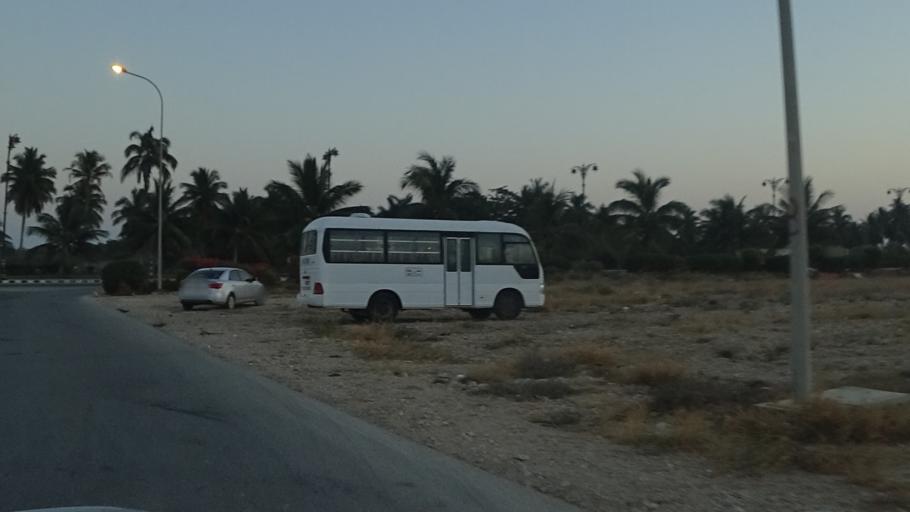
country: OM
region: Zufar
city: Salalah
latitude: 17.0447
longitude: 54.2066
